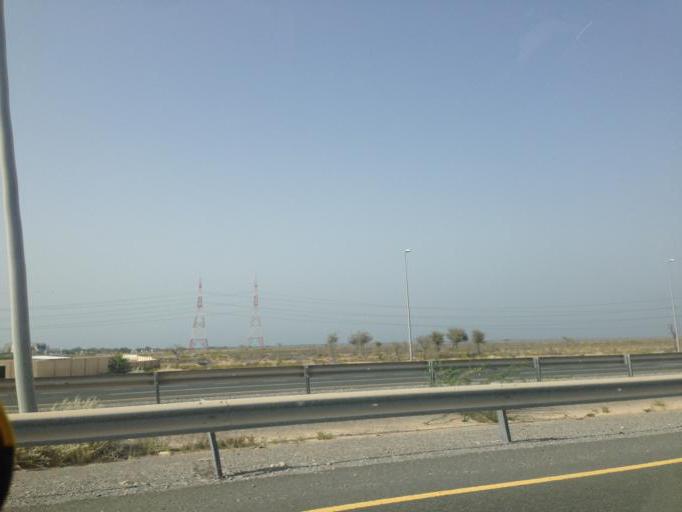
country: OM
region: Al Batinah
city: Barka'
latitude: 23.6995
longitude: 57.9869
